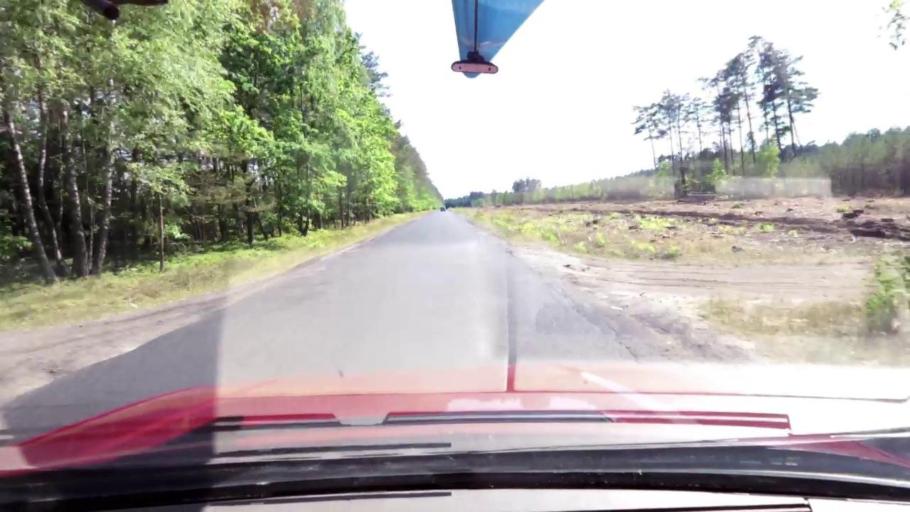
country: PL
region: Pomeranian Voivodeship
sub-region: Powiat slupski
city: Kepice
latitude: 54.3006
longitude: 16.9613
